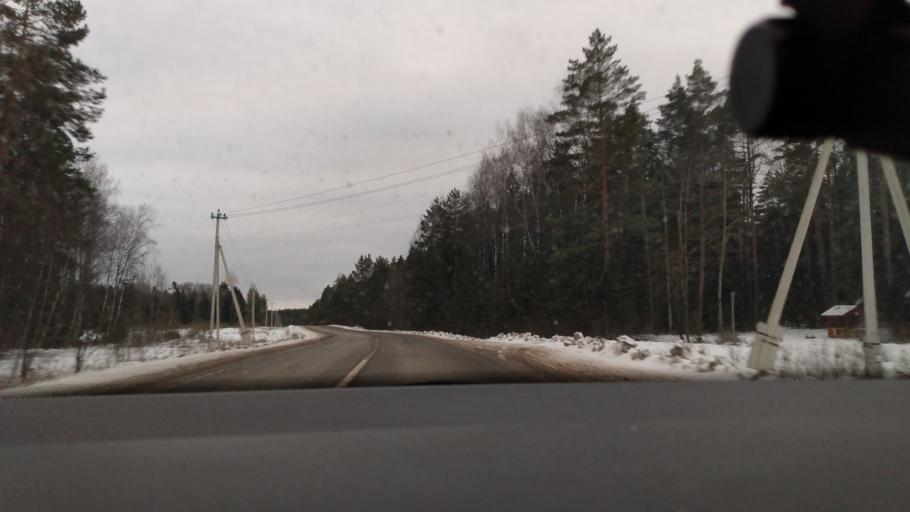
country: RU
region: Moskovskaya
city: Yegor'yevsk
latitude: 55.3265
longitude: 39.0727
